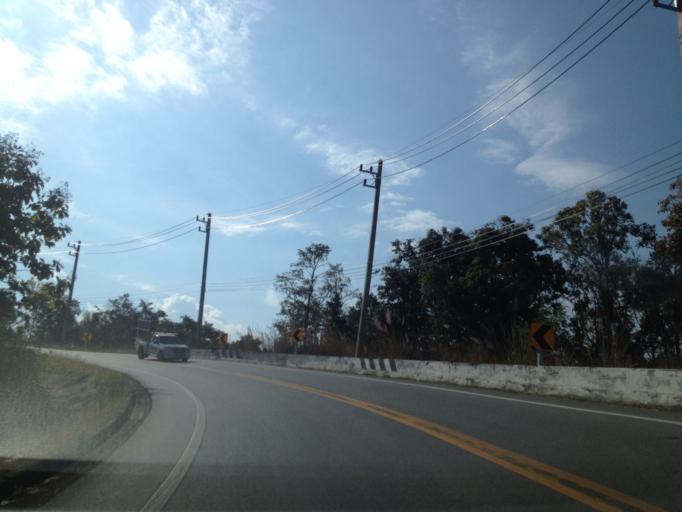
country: TH
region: Mae Hong Son
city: Ban Huai I Huak
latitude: 18.1461
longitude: 98.2629
